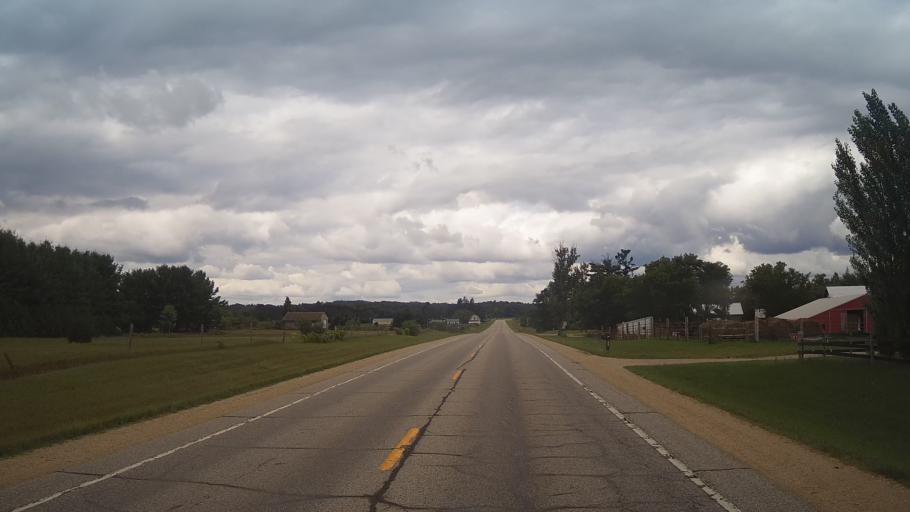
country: US
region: Wisconsin
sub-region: Waushara County
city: Wautoma
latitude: 44.0562
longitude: -89.3654
